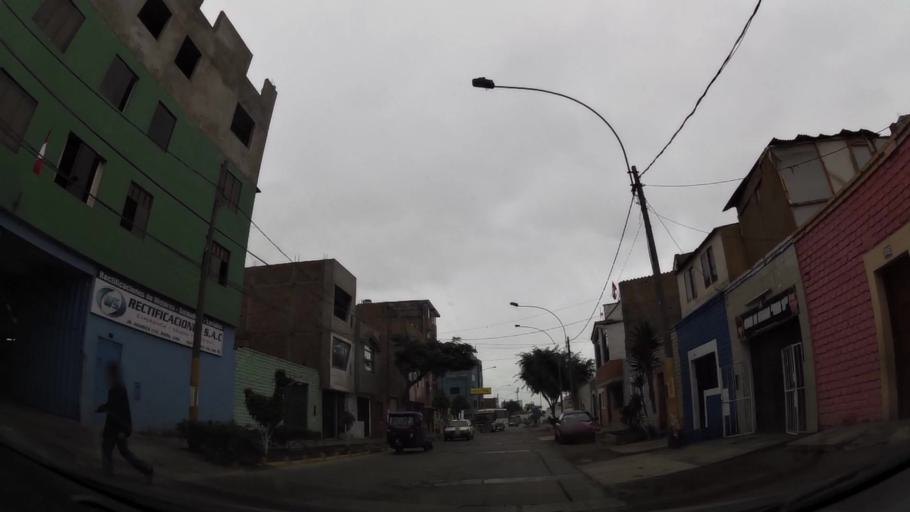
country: PE
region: Lima
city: Lima
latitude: -12.0590
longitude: -77.0523
